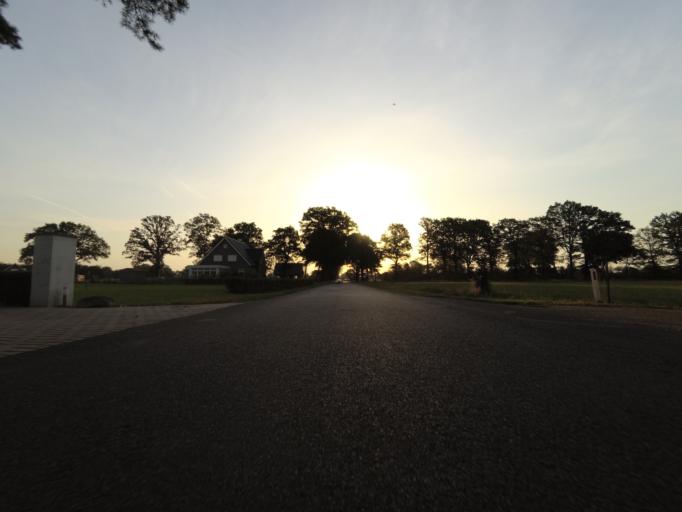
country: NL
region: Overijssel
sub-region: Gemeente Wierden
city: Wierden
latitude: 52.3393
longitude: 6.5273
